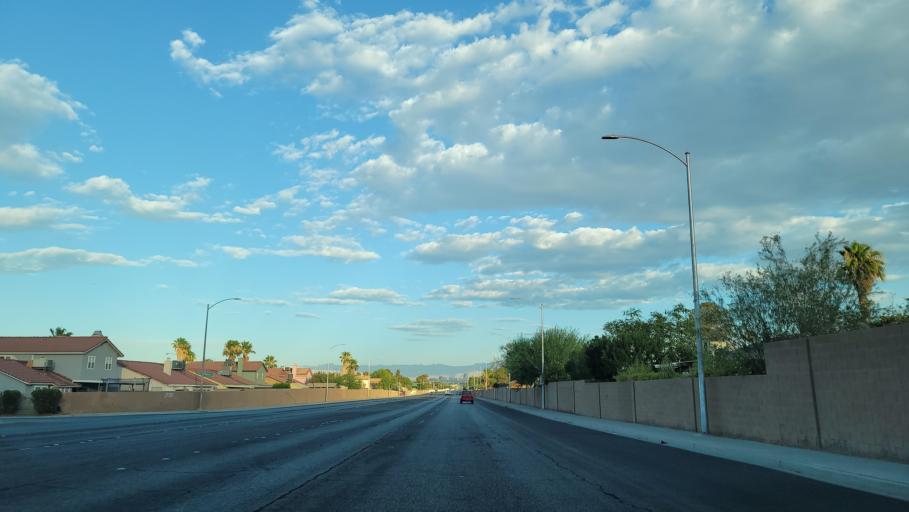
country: US
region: Nevada
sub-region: Clark County
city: Sunrise Manor
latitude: 36.1745
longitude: -115.0444
